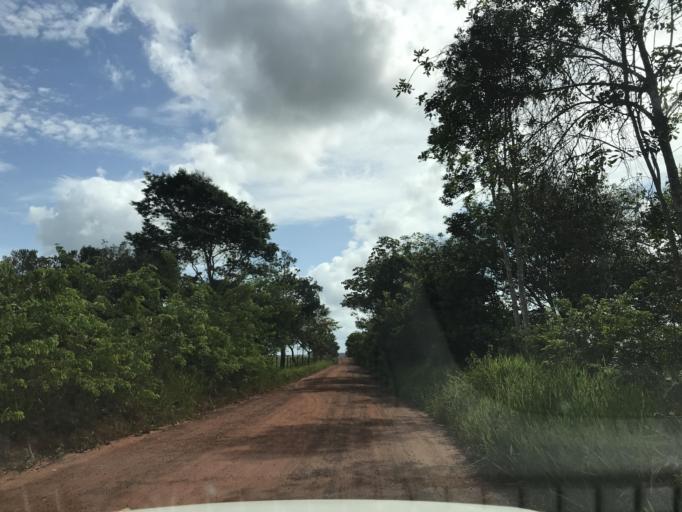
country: BR
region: Bahia
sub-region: Entre Rios
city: Entre Rios
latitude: -12.1718
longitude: -38.1075
